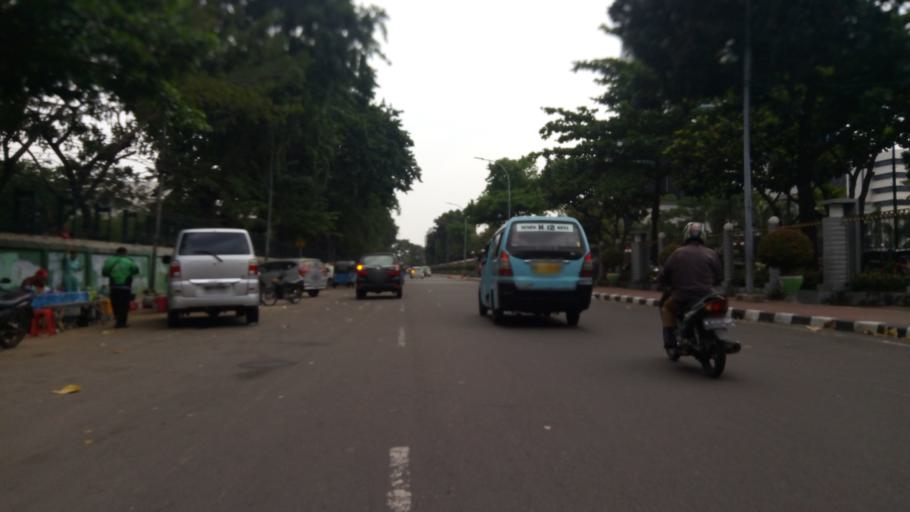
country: ID
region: Jakarta Raya
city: Jakarta
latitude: -6.1734
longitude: 106.8380
